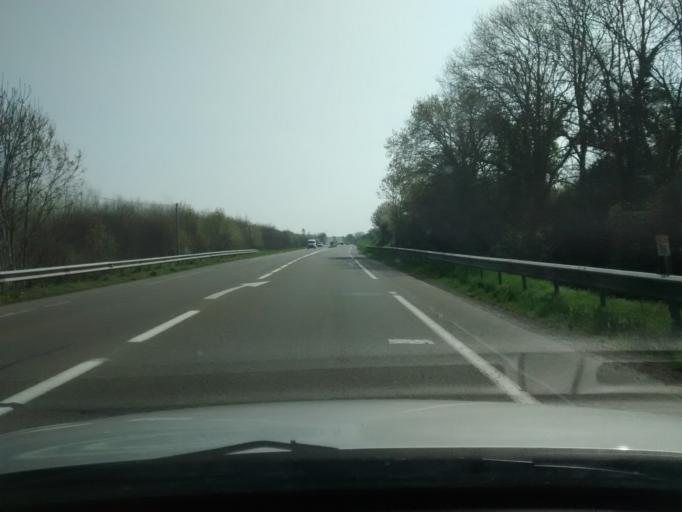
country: FR
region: Pays de la Loire
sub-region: Departement de la Mayenne
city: Argentre
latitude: 48.0671
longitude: -0.6584
